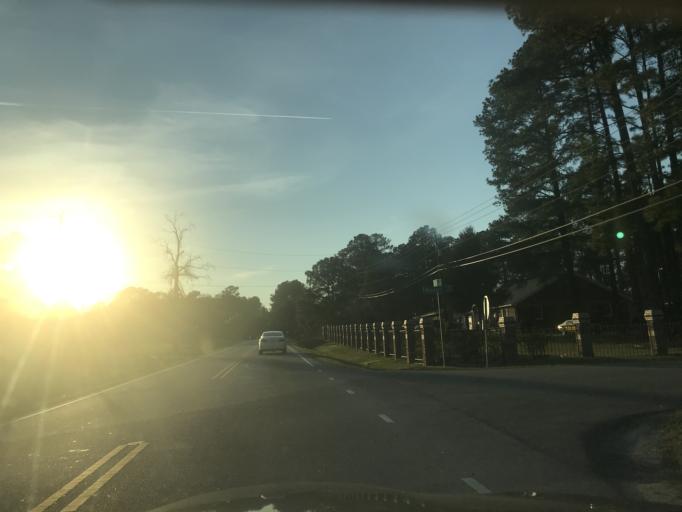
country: US
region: North Carolina
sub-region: Wake County
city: Knightdale
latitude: 35.7555
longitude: -78.5387
